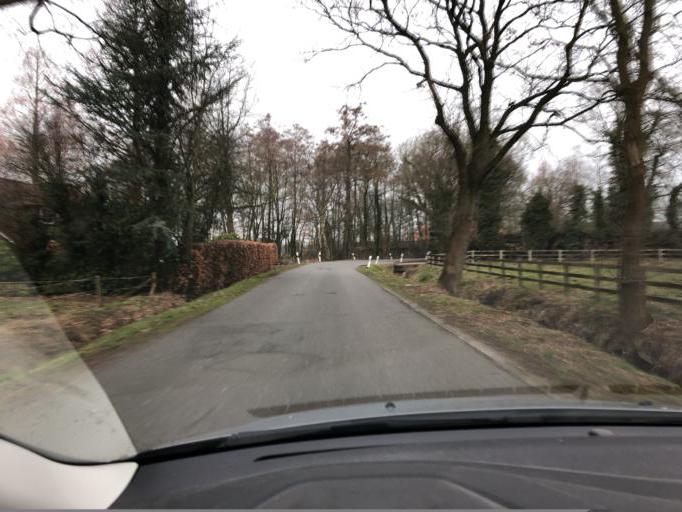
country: DE
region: Lower Saxony
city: Bad Zwischenahn
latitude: 53.1714
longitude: 8.0293
